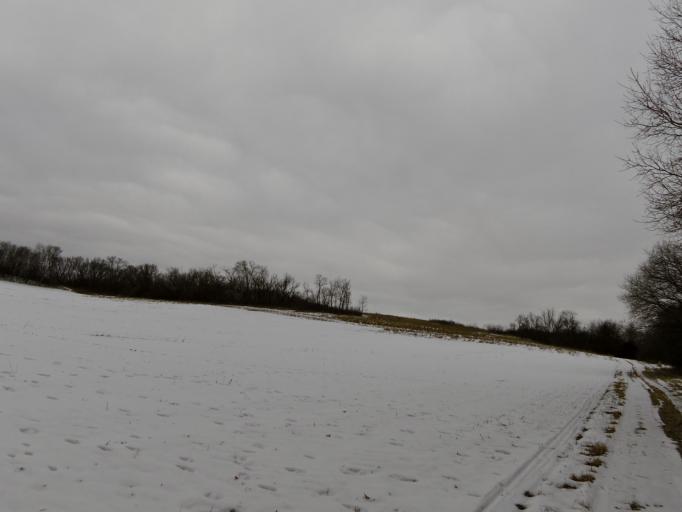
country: US
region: Wisconsin
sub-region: Pierce County
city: Prescott
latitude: 44.7990
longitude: -92.8197
